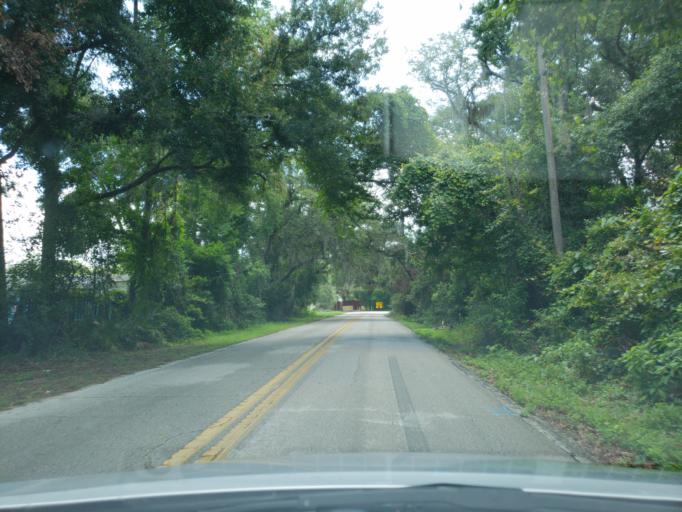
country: US
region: Florida
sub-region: Hillsborough County
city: Riverview
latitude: 27.8790
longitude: -82.3155
